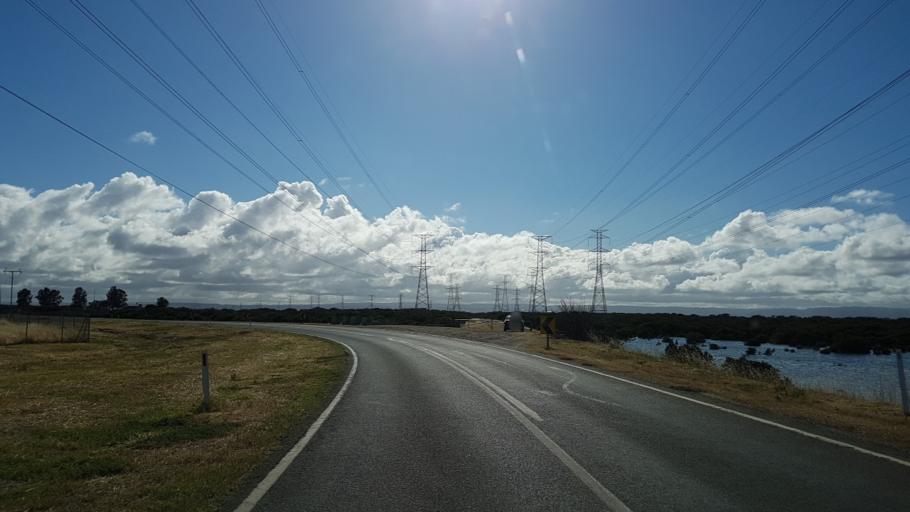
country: AU
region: South Australia
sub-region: Port Adelaide Enfield
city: Birkenhead
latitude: -34.8074
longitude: 138.5375
